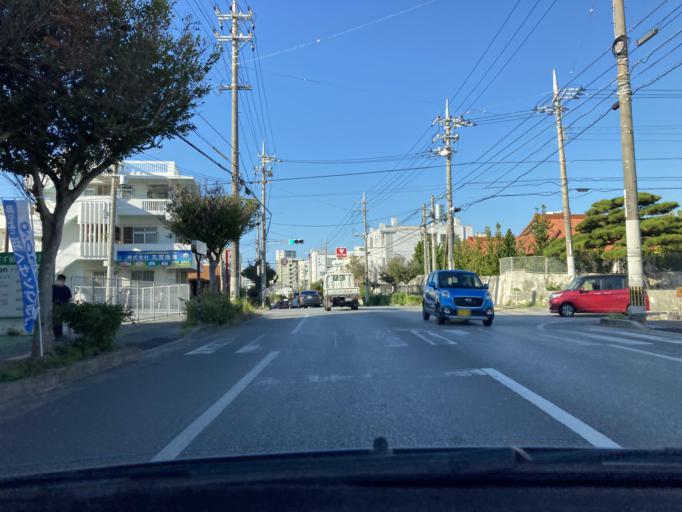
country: JP
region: Okinawa
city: Ginowan
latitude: 26.2540
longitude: 127.7138
